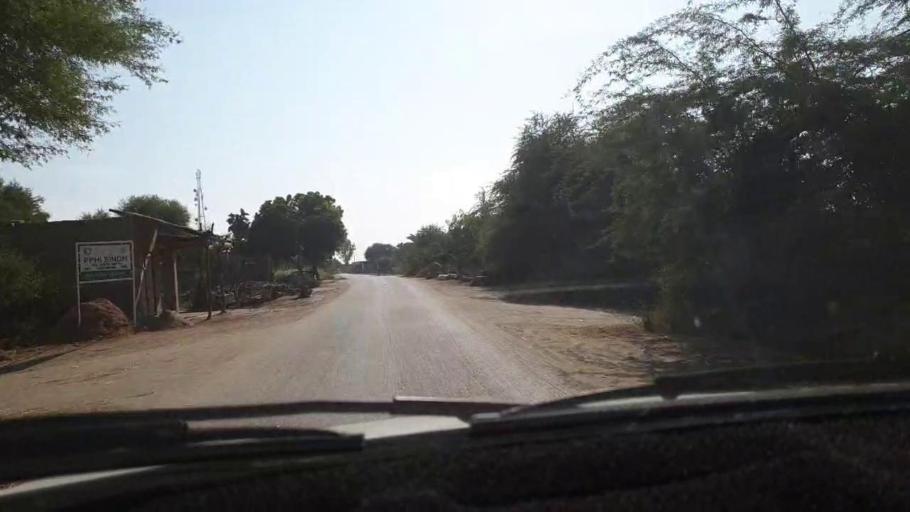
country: PK
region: Sindh
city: Bulri
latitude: 24.9615
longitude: 68.4202
